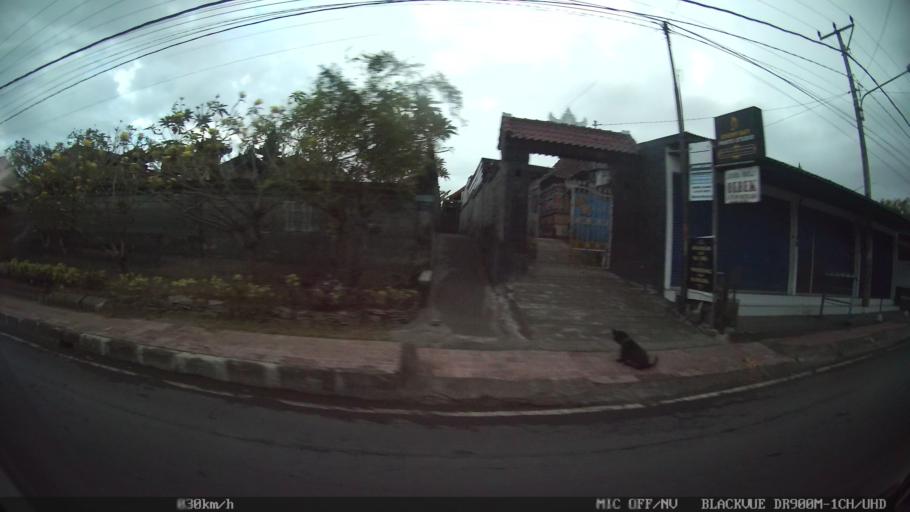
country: ID
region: Bali
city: Banjar Pasekan
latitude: -8.6226
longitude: 115.2841
